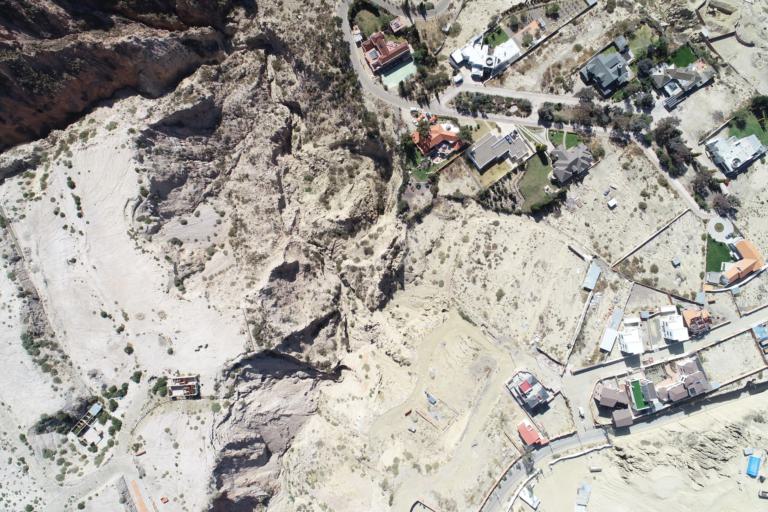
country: BO
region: La Paz
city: La Paz
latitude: -16.5574
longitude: -68.1057
